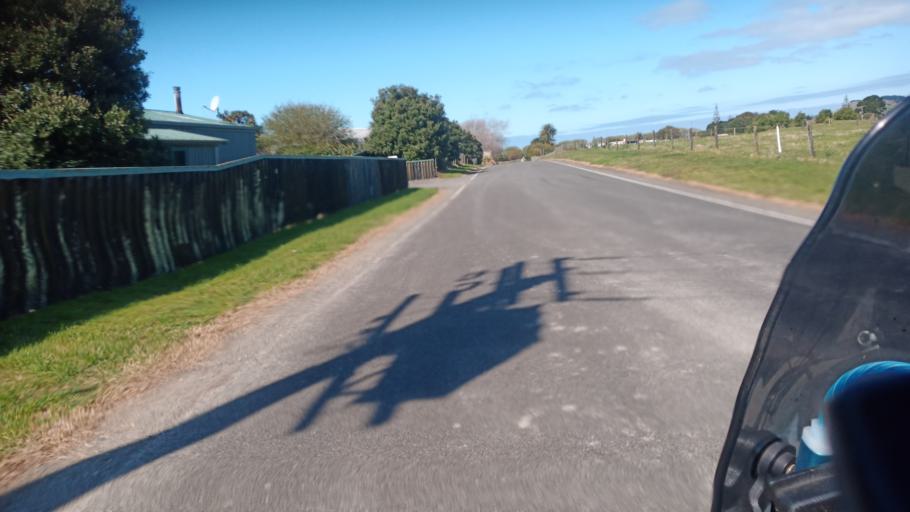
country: NZ
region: Gisborne
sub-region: Gisborne District
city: Gisborne
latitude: -39.0511
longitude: 177.8755
